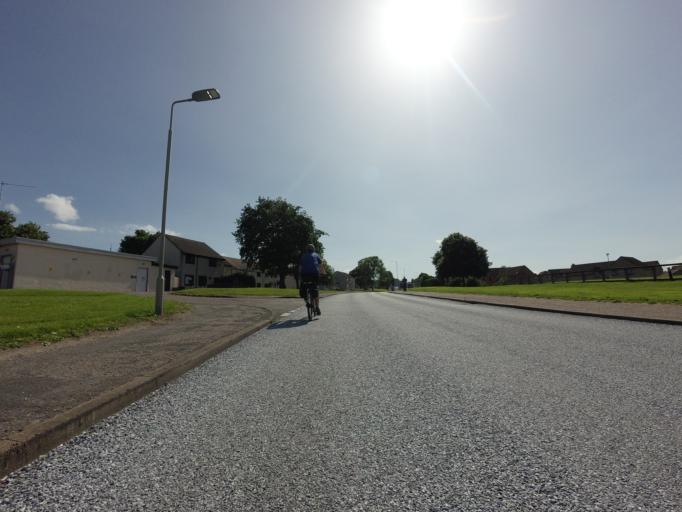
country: GB
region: Scotland
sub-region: Highland
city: Inverness
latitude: 57.4818
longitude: -4.1496
